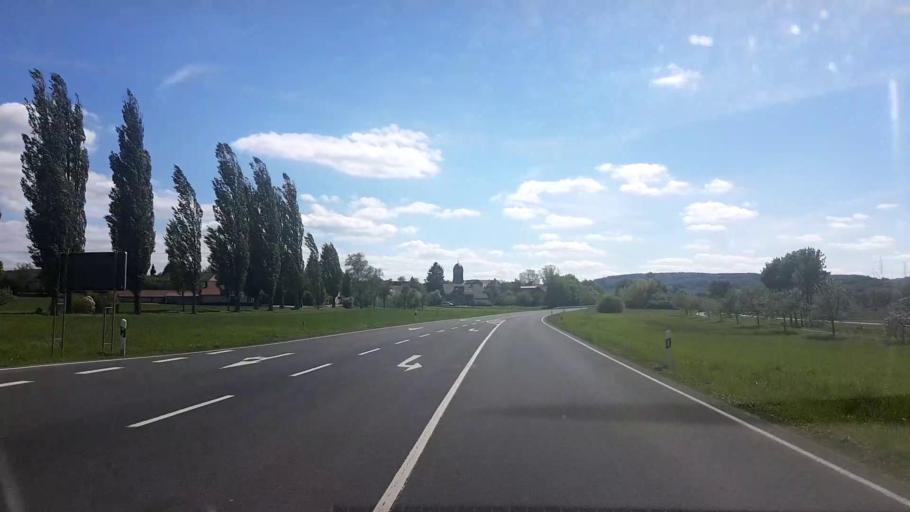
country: DE
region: Bavaria
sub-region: Regierungsbezirk Unterfranken
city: Untermerzbach
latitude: 50.1057
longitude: 10.8668
